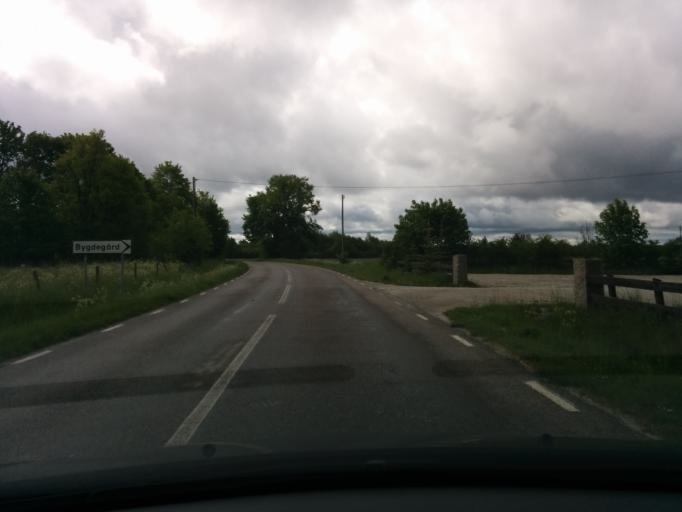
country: SE
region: Gotland
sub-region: Gotland
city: Slite
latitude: 57.5849
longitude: 18.7289
